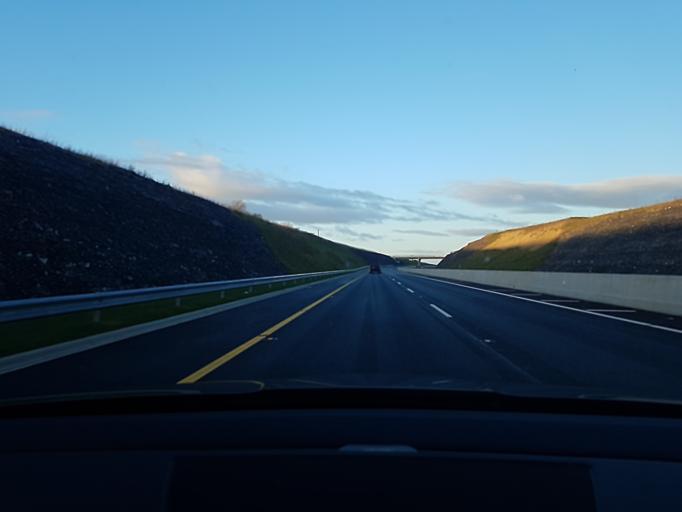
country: IE
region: Connaught
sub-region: County Galway
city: Athenry
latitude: 53.3446
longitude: -8.8016
